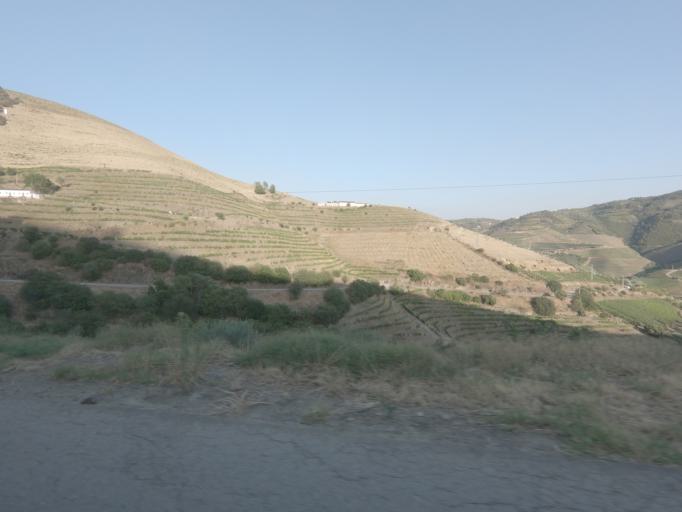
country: PT
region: Vila Real
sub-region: Sabrosa
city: Vilela
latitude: 41.1669
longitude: -7.6264
